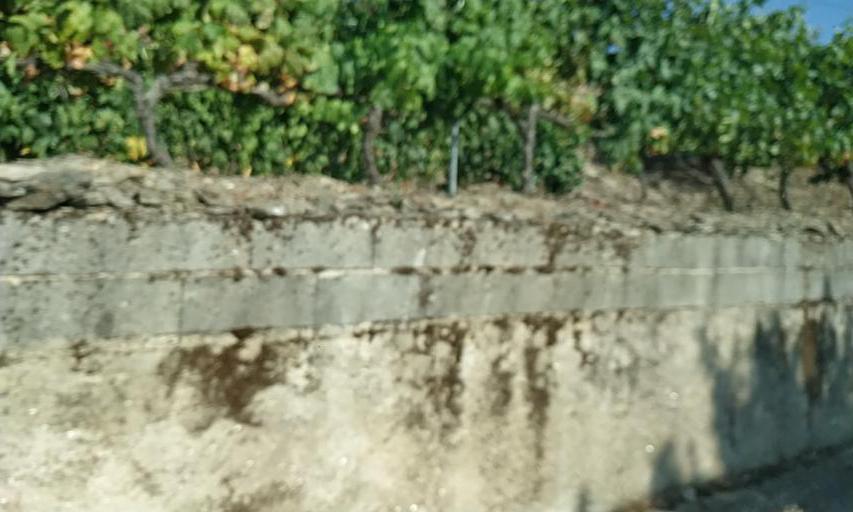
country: PT
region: Viseu
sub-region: Sao Joao da Pesqueira
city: Sao Joao da Pesqueira
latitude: 41.1853
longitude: -7.4403
